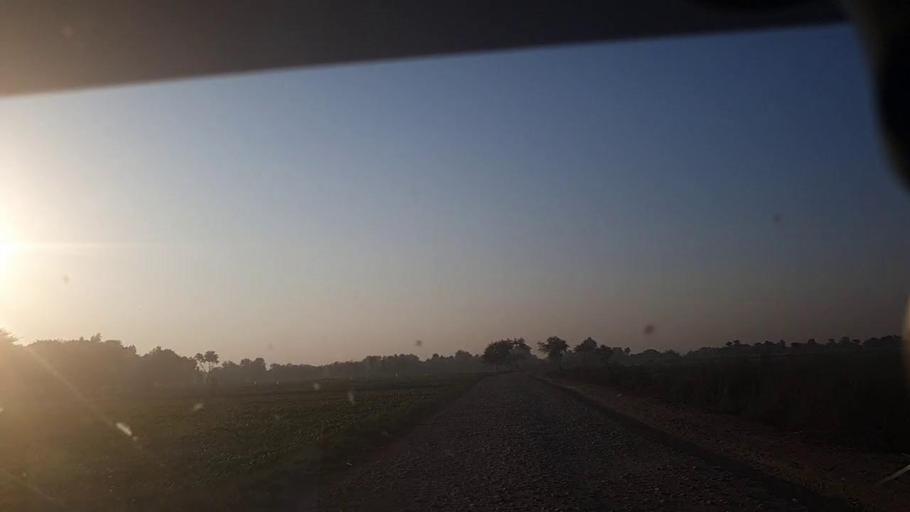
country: PK
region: Sindh
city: Sobhadero
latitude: 27.3614
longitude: 68.4172
